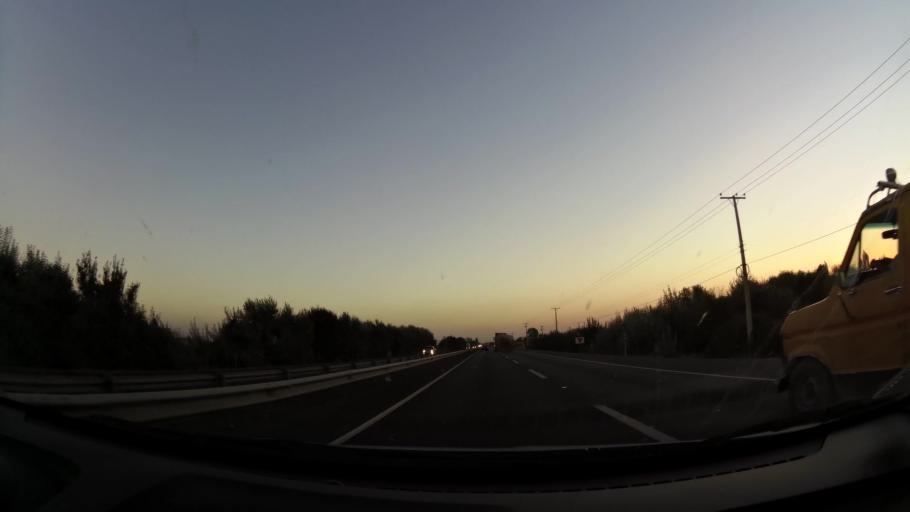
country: CL
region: Maule
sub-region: Provincia de Linares
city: Longavi
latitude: -35.9251
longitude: -71.6601
